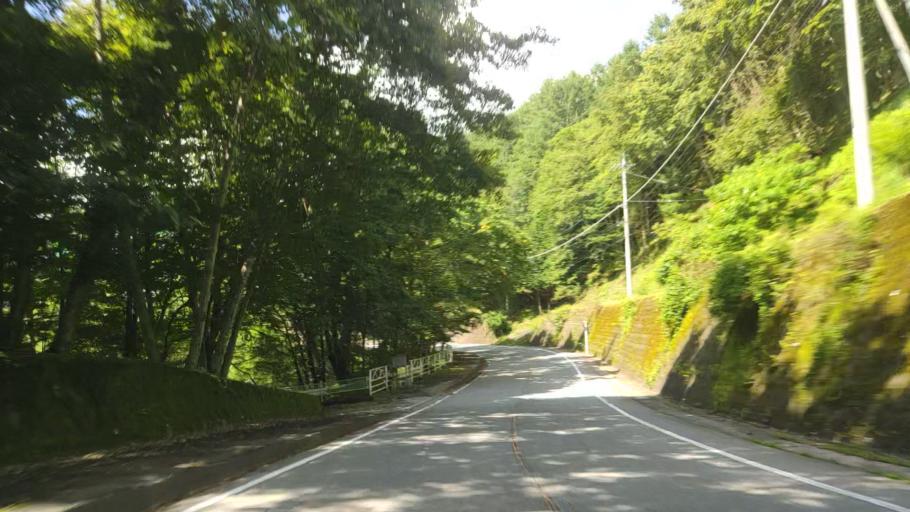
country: JP
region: Yamanashi
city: Enzan
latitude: 35.8529
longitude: 138.7584
